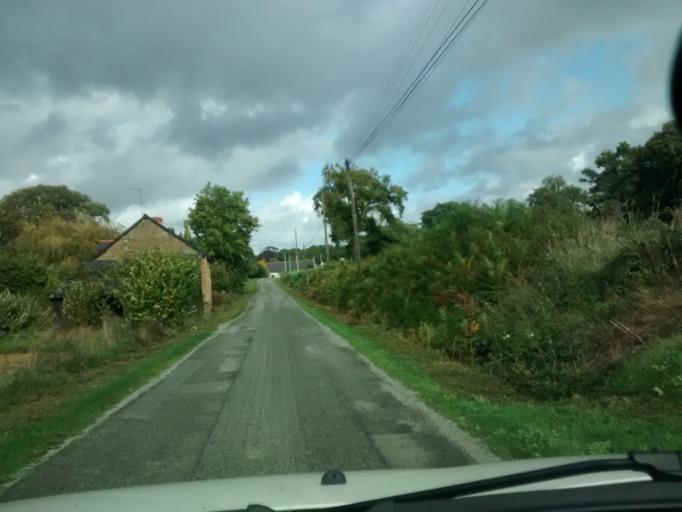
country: FR
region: Brittany
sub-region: Departement d'Ille-et-Vilaine
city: Chateaubourg
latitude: 48.1348
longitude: -1.4193
